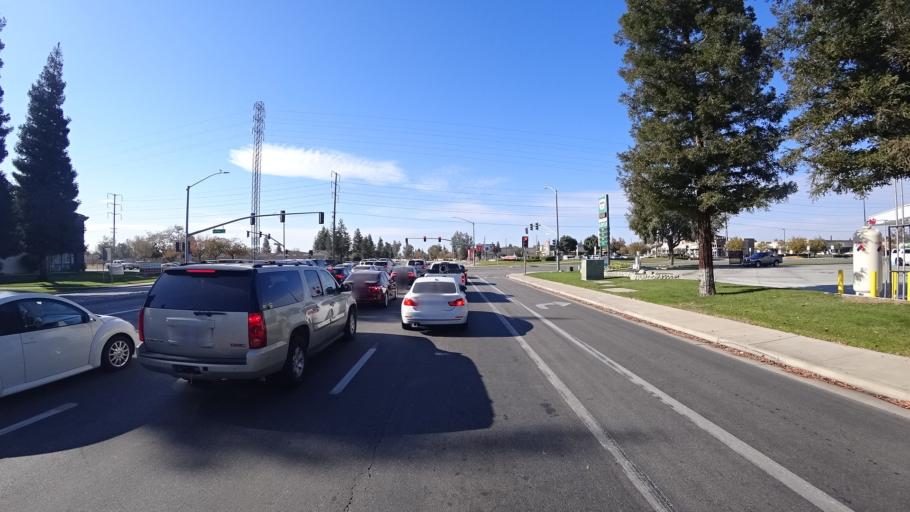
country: US
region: California
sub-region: Kern County
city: Greenacres
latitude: 35.4016
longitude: -119.0916
